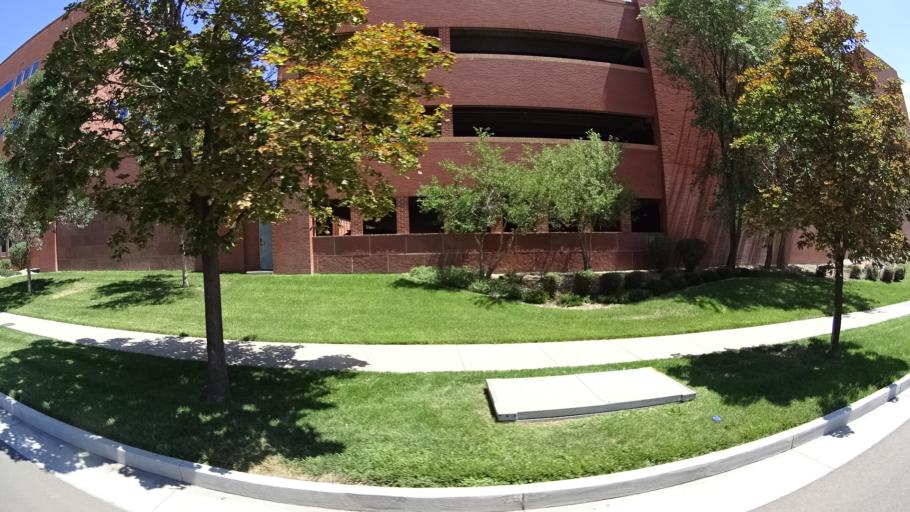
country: US
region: Colorado
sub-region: El Paso County
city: Colorado Springs
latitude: 38.8237
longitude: -104.8221
